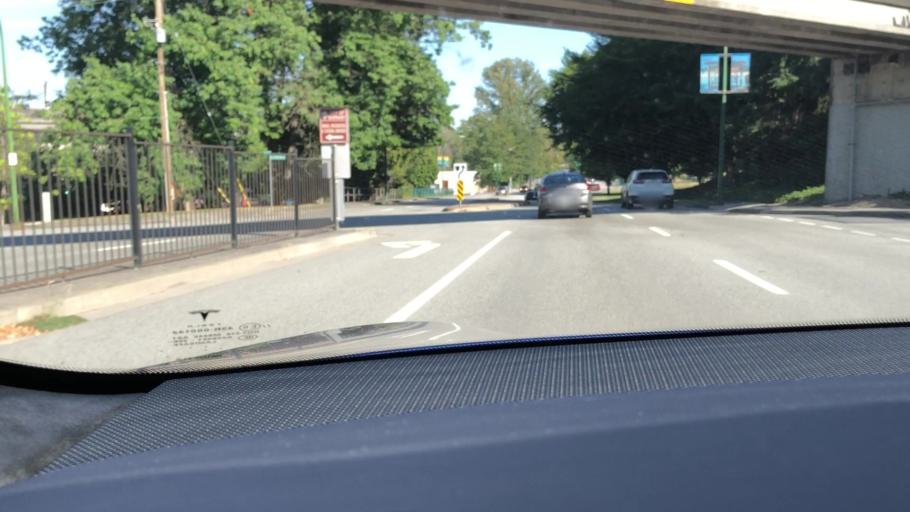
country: CA
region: British Columbia
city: Burnaby
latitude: 49.2441
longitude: -122.9724
